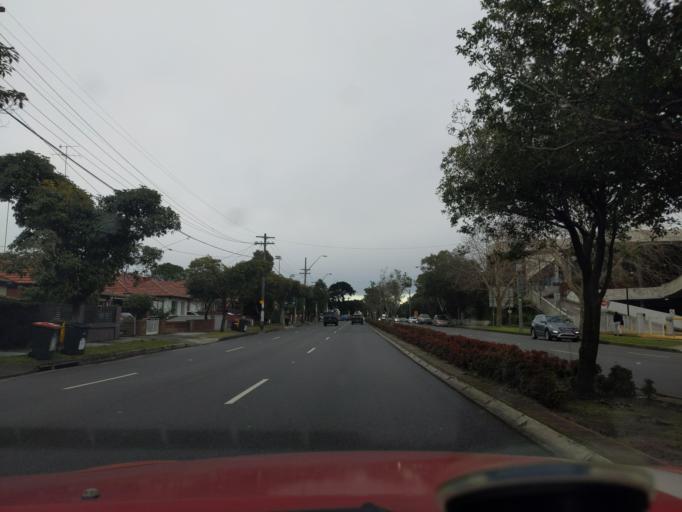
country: AU
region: New South Wales
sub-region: Randwick
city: Maroubra
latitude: -33.9460
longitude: 151.2254
